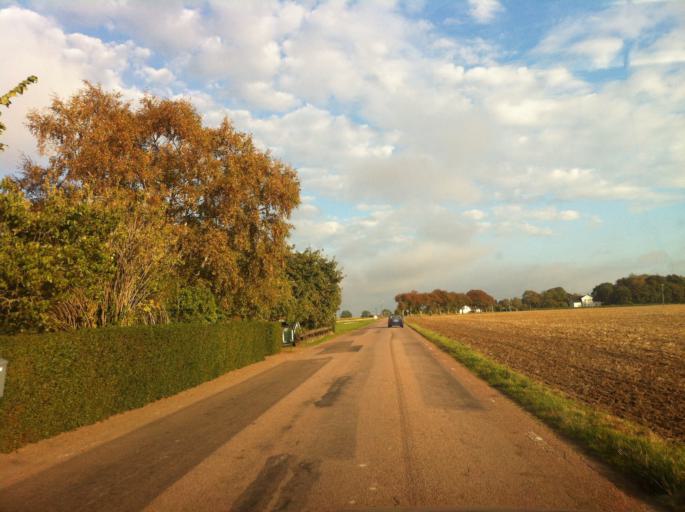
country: SE
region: Skane
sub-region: Helsingborg
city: Barslov
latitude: 55.9916
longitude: 12.8257
